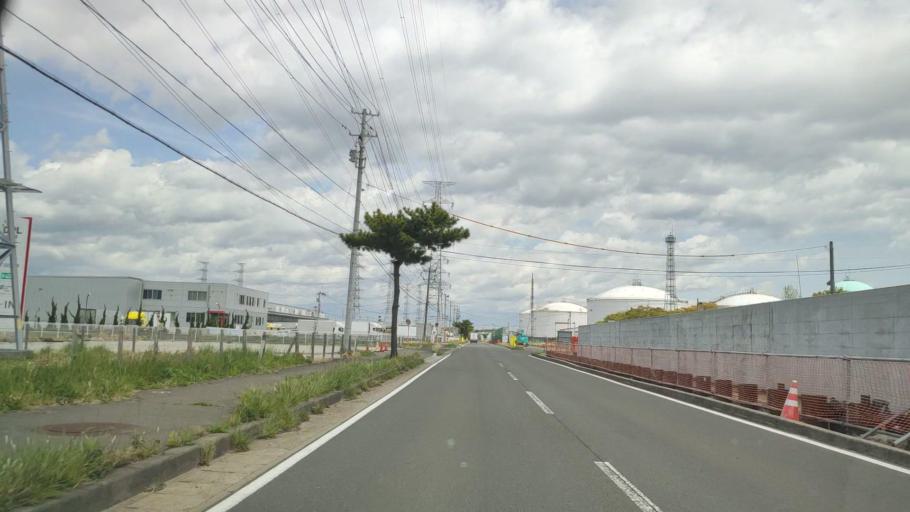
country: JP
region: Miyagi
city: Shiogama
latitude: 38.2794
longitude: 141.0212
